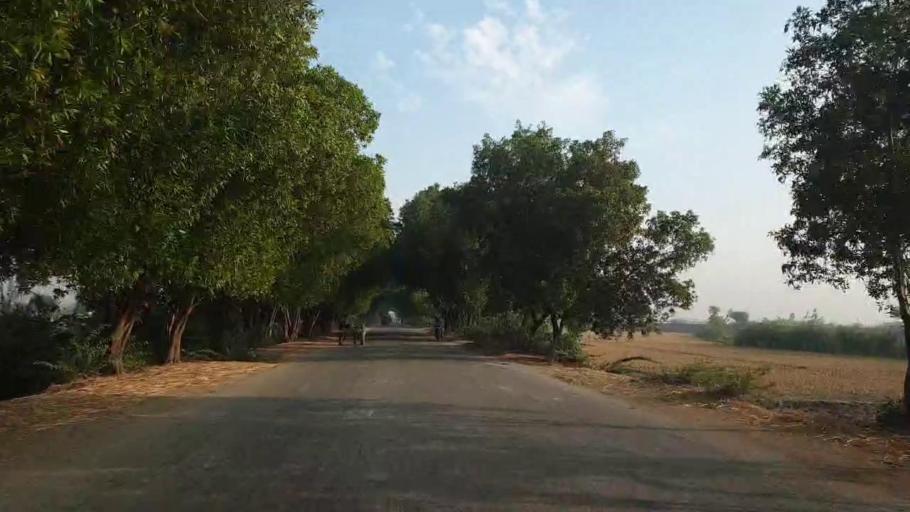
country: PK
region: Sindh
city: Tando Bago
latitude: 24.7717
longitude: 68.9590
